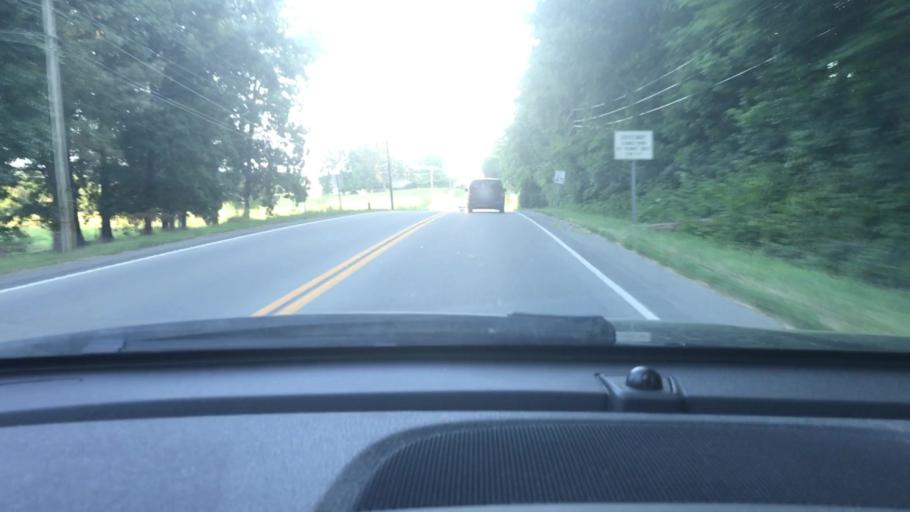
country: US
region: Tennessee
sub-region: Dickson County
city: Dickson
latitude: 36.0984
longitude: -87.3751
